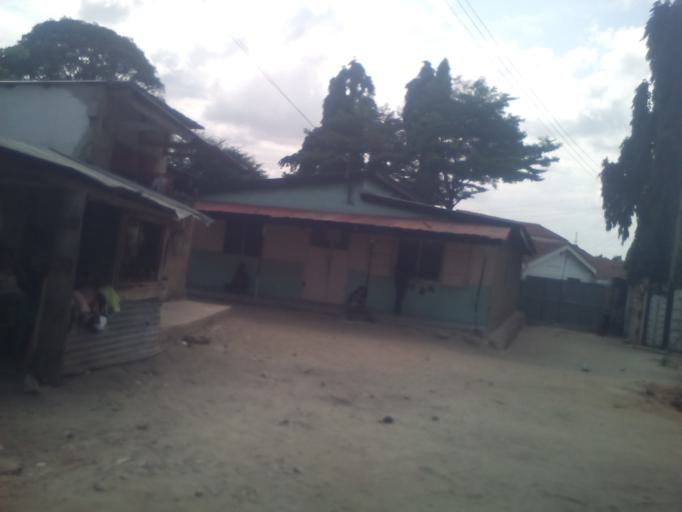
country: TZ
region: Dar es Salaam
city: Dar es Salaam
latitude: -6.8449
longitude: 39.2772
